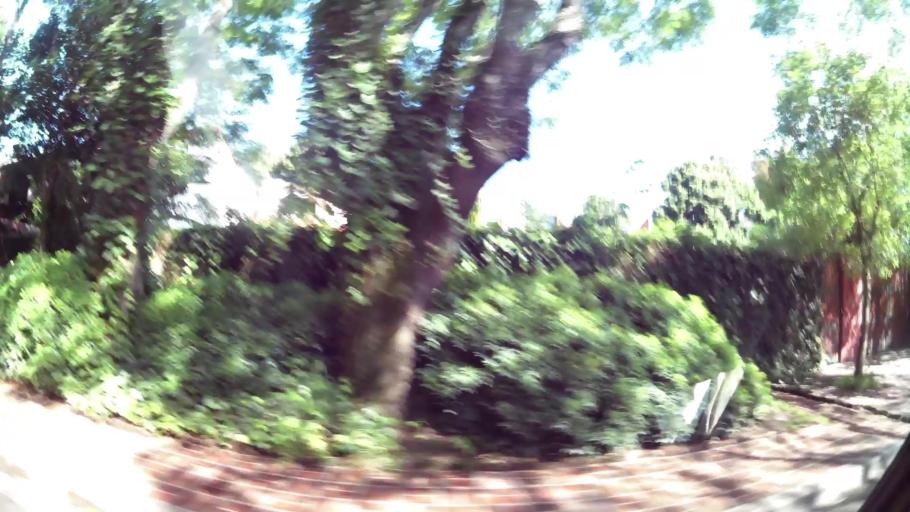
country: AR
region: Buenos Aires
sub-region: Partido de Tigre
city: Tigre
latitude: -34.4825
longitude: -58.5739
